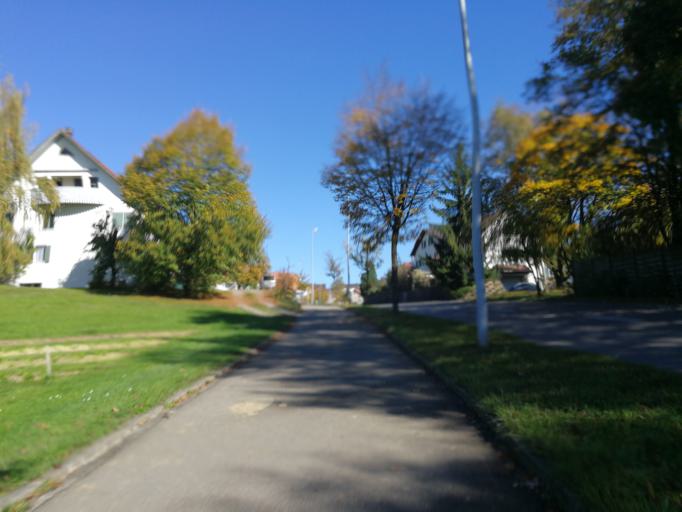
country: CH
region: Zurich
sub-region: Bezirk Hinwil
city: Gruet
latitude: 47.3094
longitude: 8.7776
